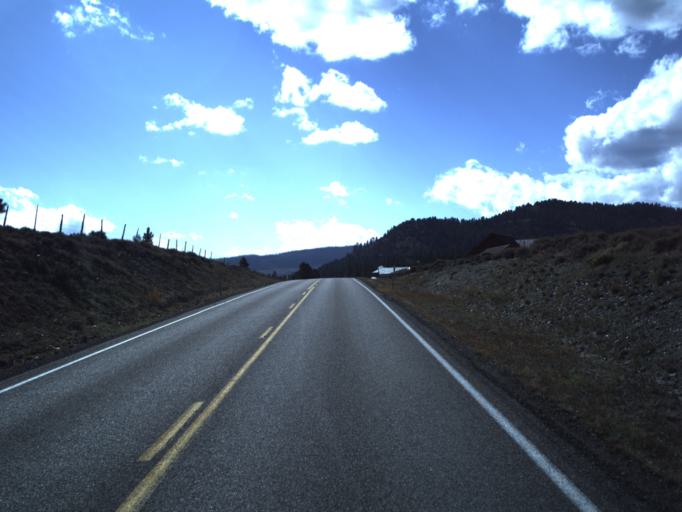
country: US
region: Utah
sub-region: Iron County
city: Parowan
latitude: 37.7047
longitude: -112.6422
